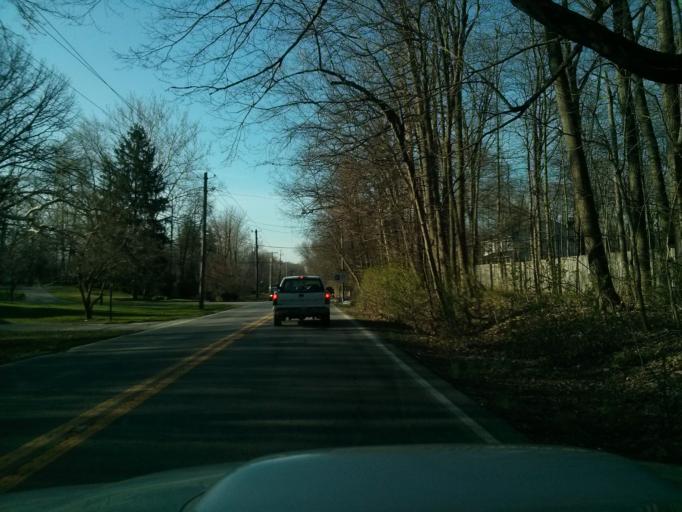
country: US
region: Indiana
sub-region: Marion County
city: Meridian Hills
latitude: 39.8973
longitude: -86.1459
